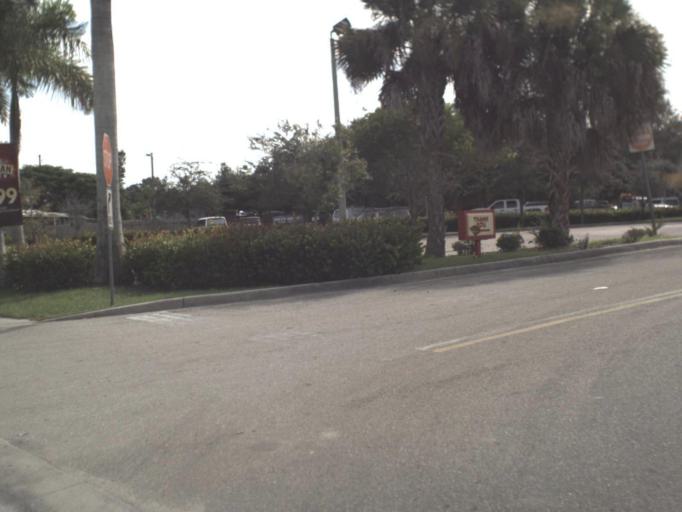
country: US
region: Florida
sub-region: Lee County
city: Tice
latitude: 26.6697
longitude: -81.8242
